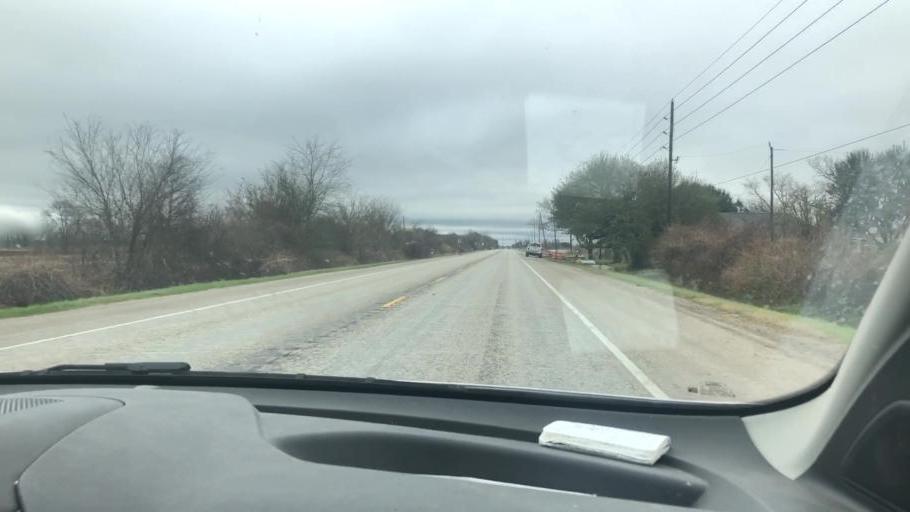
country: US
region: Texas
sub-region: Wharton County
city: Wharton
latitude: 29.2656
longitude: -96.0572
